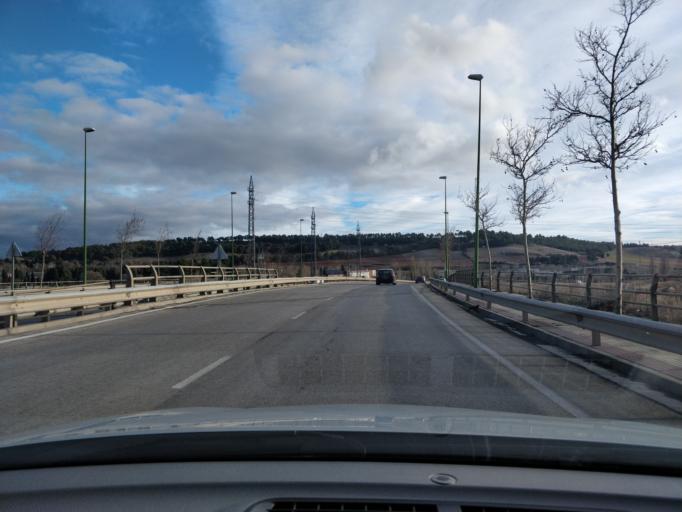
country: ES
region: Castille and Leon
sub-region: Provincia de Burgos
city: Burgos
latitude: 42.3615
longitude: -3.7091
